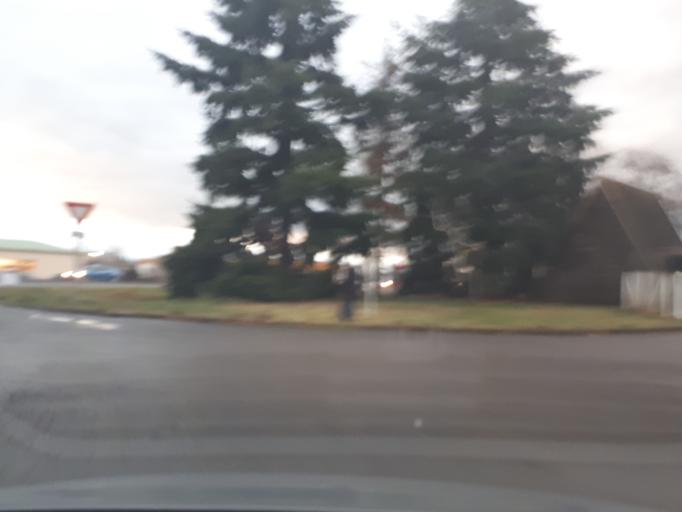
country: FR
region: Rhone-Alpes
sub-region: Departement de la Loire
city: Feurs
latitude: 45.7234
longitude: 4.2264
